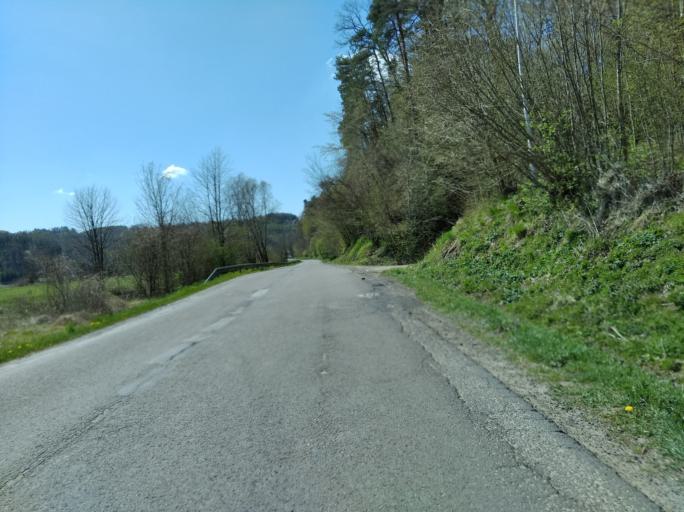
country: PL
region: Subcarpathian Voivodeship
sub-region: Powiat brzozowski
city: Dydnia
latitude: 49.7021
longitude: 22.1941
